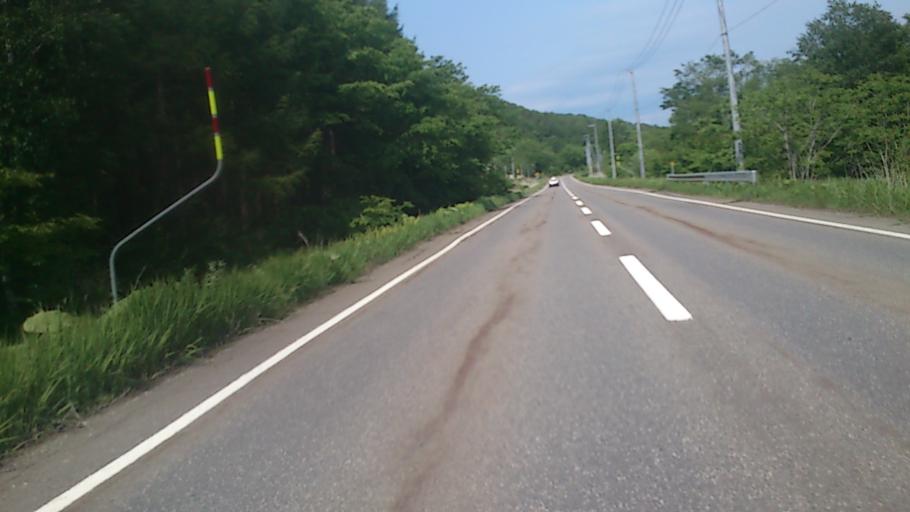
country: JP
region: Hokkaido
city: Otofuke
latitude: 43.2619
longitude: 143.5768
